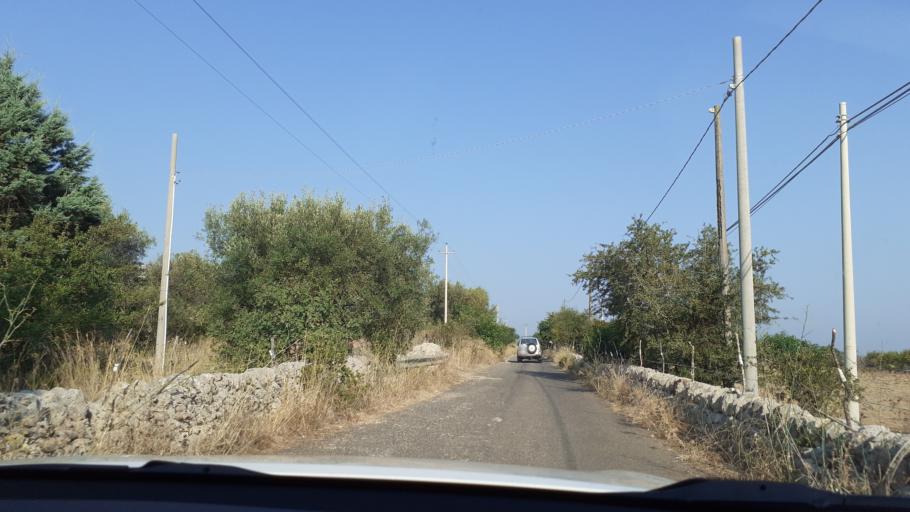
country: IT
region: Sicily
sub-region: Provincia di Siracusa
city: Cassibile
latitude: 36.9813
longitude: 15.1666
